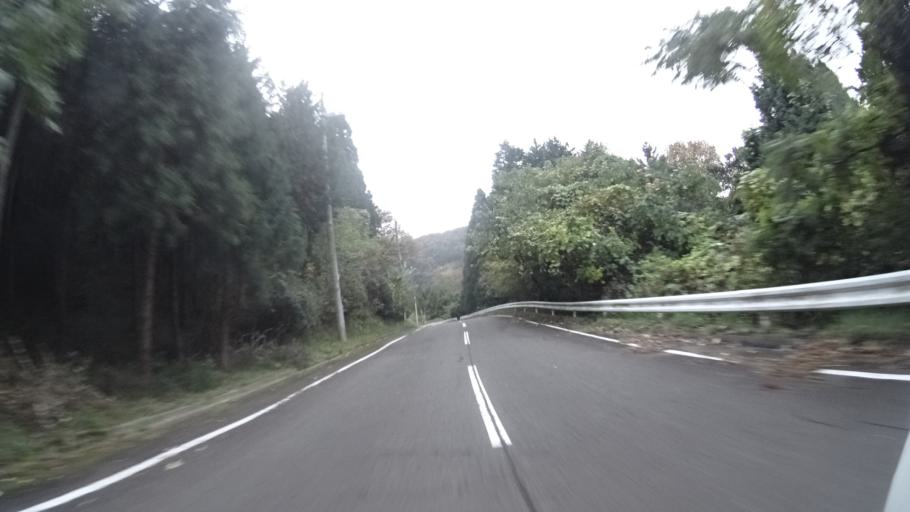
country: JP
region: Kyoto
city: Maizuru
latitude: 35.5655
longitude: 135.4584
